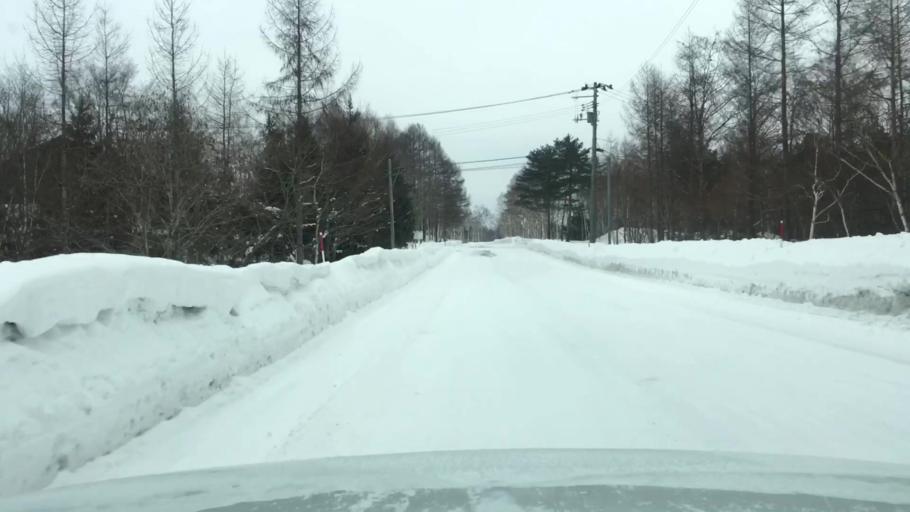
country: JP
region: Akita
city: Hanawa
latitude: 40.0049
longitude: 140.9807
